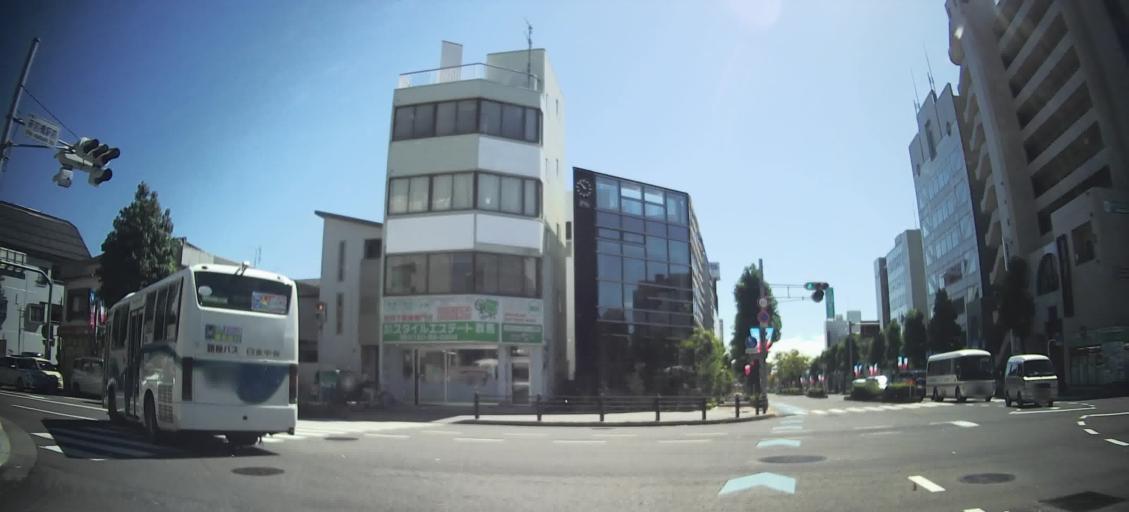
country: JP
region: Gunma
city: Maebashi-shi
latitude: 36.3783
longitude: 139.0483
